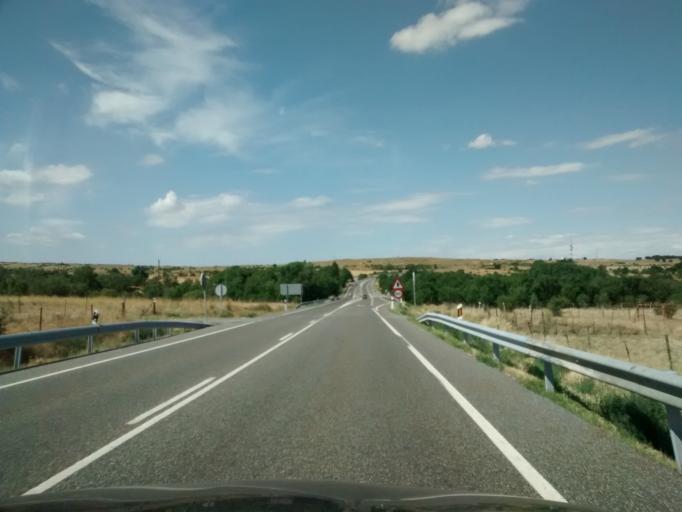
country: ES
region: Castille and Leon
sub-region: Provincia de Segovia
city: Santo Domingo de Piron
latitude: 41.0115
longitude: -3.9812
